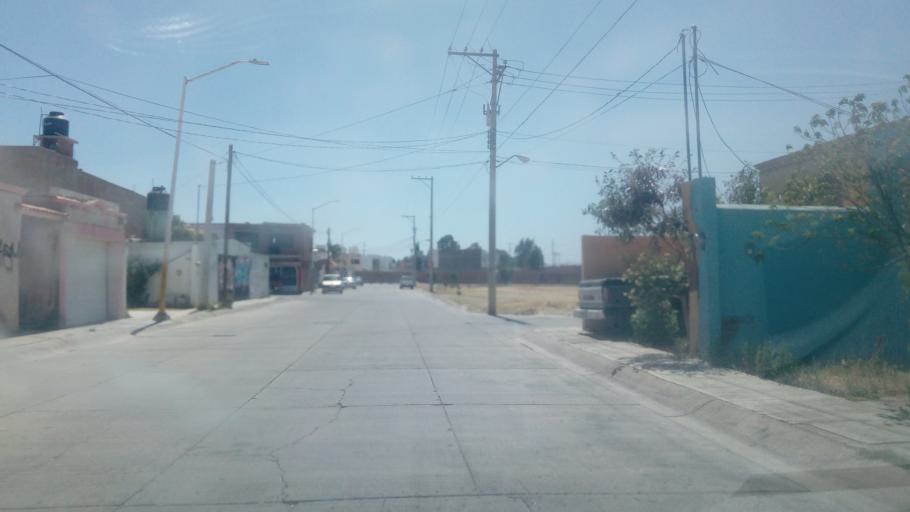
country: MX
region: Durango
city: Victoria de Durango
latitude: 24.0054
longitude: -104.6296
